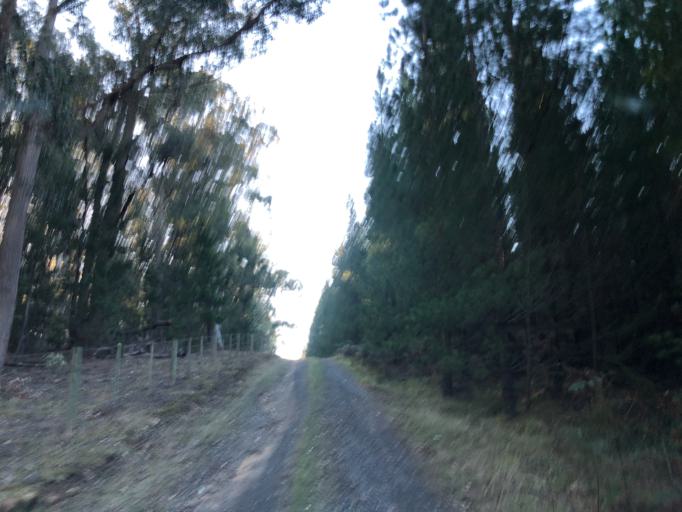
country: AU
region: Victoria
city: Brown Hill
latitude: -37.5068
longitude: 144.1521
